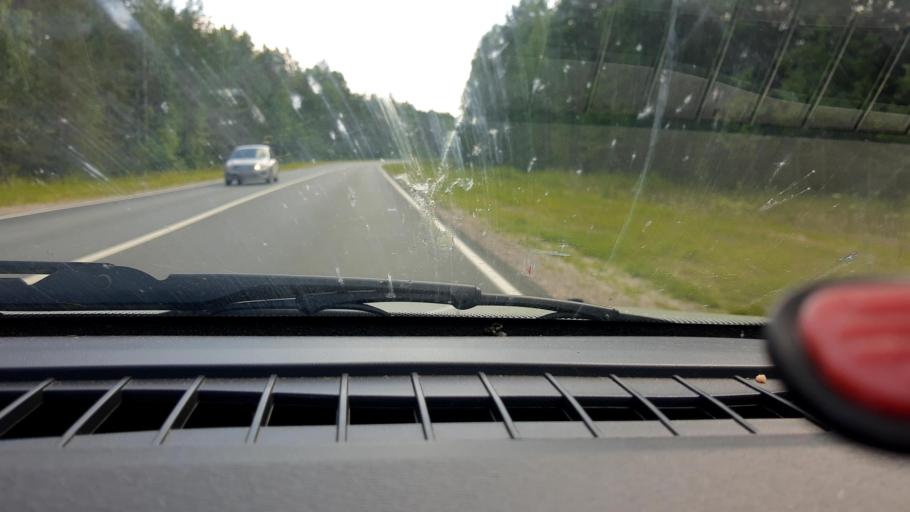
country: RU
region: Nizjnij Novgorod
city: Krasnyye Baki
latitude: 57.2203
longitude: 45.4851
